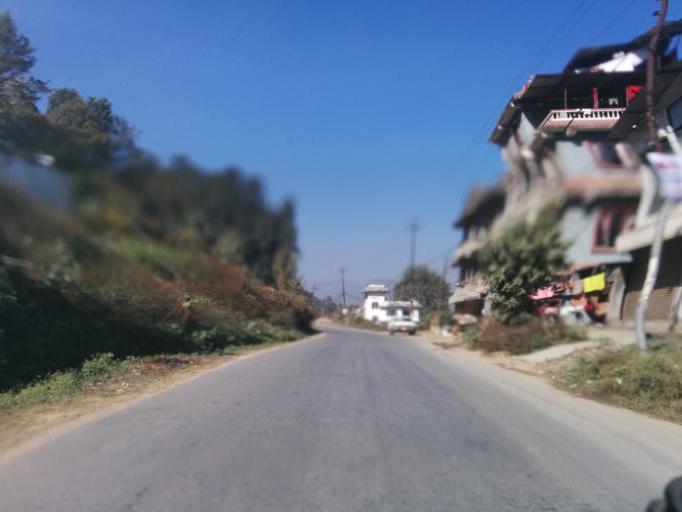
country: NP
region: Central Region
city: Kirtipur
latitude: 27.6798
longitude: 85.2776
